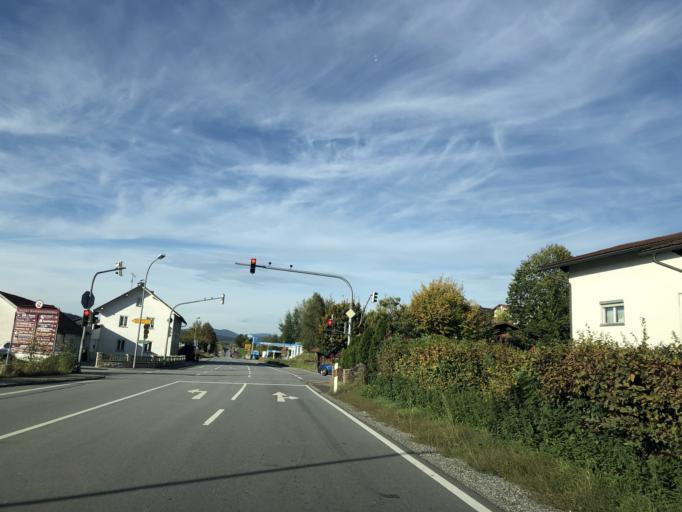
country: DE
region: Bavaria
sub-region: Lower Bavaria
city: Ruhmannsfelden
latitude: 48.9834
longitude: 12.9811
